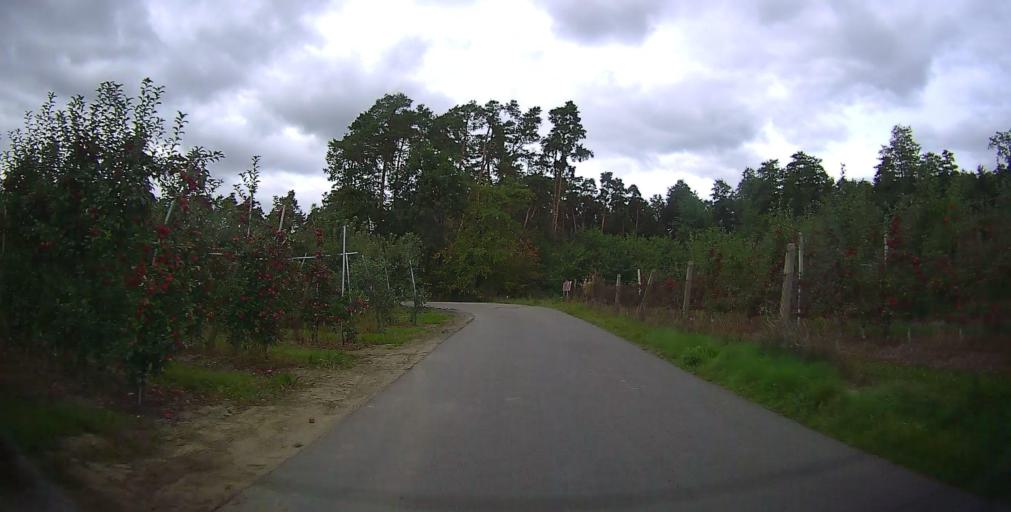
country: PL
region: Masovian Voivodeship
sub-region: Powiat grojecki
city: Goszczyn
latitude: 51.7745
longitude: 20.8640
